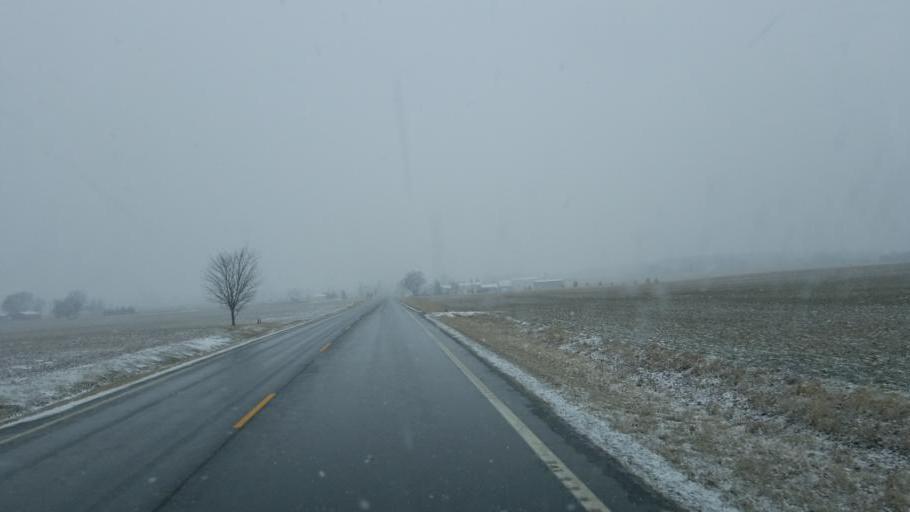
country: US
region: Ohio
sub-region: Defiance County
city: Hicksville
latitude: 41.3217
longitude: -84.7475
